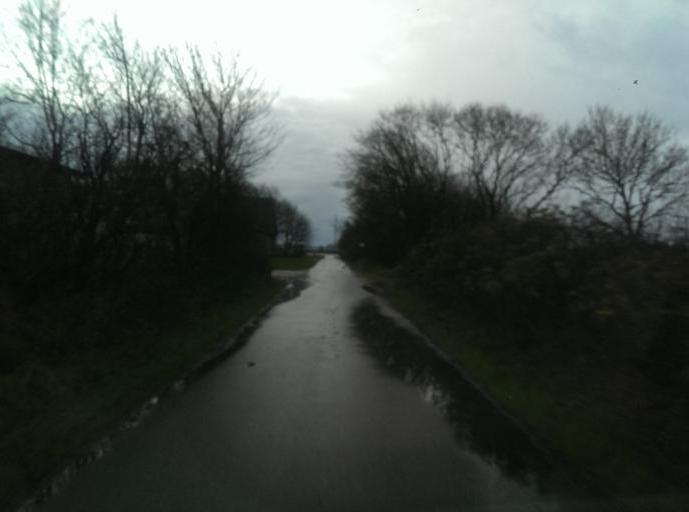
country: DK
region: South Denmark
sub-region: Esbjerg Kommune
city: Tjaereborg
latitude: 55.4523
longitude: 8.6113
